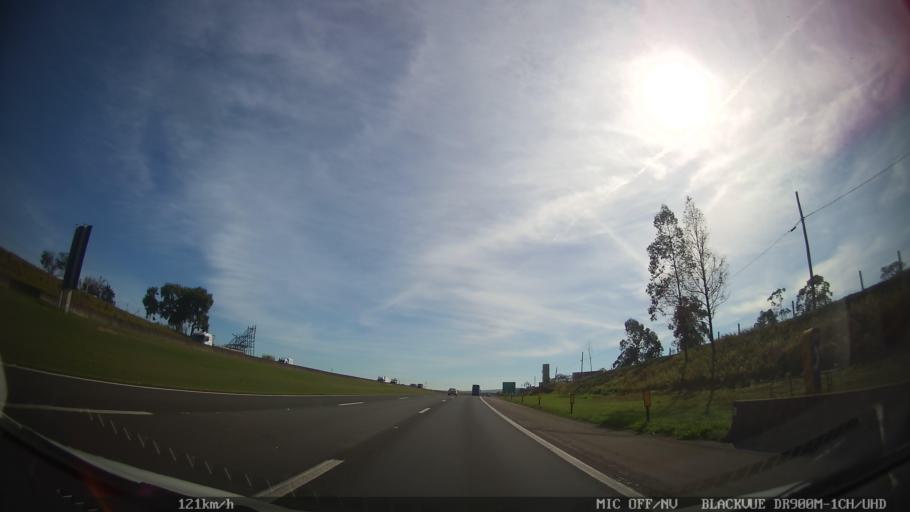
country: BR
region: Sao Paulo
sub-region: Araras
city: Araras
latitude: -22.3870
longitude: -47.3941
